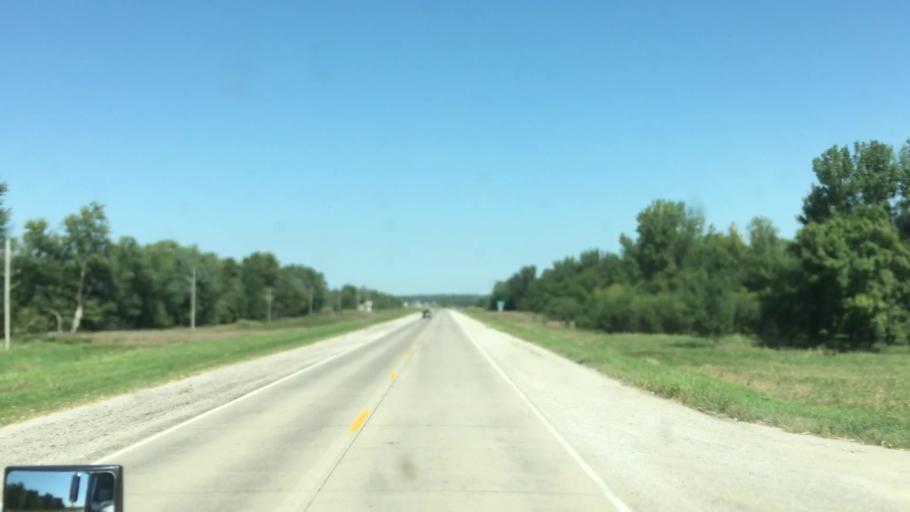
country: US
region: Iowa
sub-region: Benton County
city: Belle Plaine
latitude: 41.8619
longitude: -92.2778
